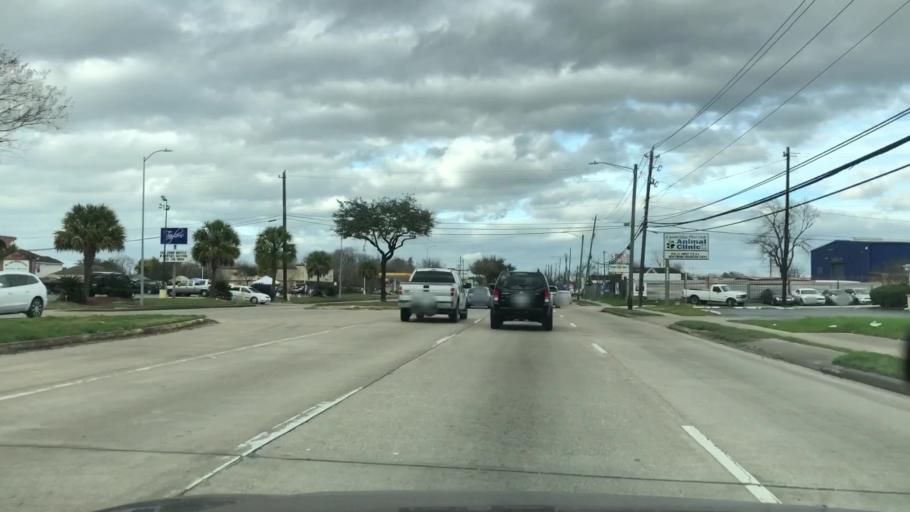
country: US
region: Texas
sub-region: Harris County
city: Bellaire
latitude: 29.6345
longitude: -95.4635
